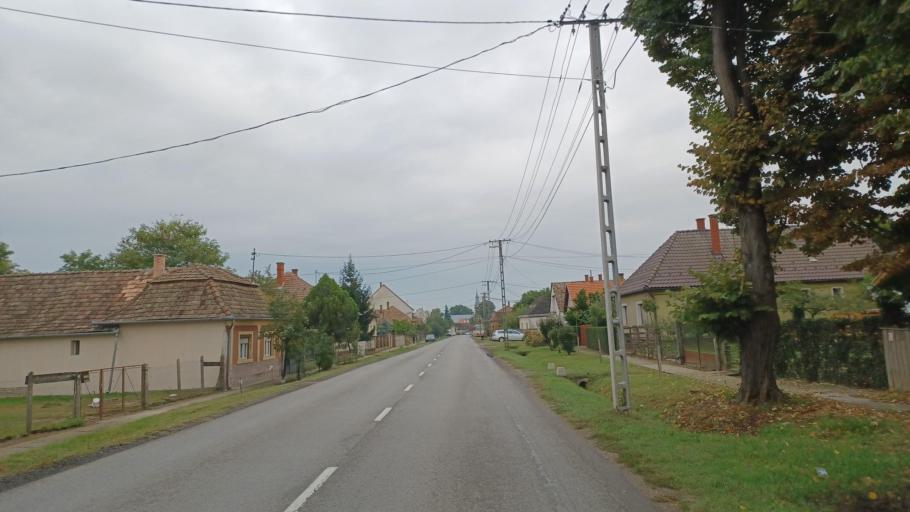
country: HU
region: Tolna
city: Nagydorog
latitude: 46.6341
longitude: 18.6538
